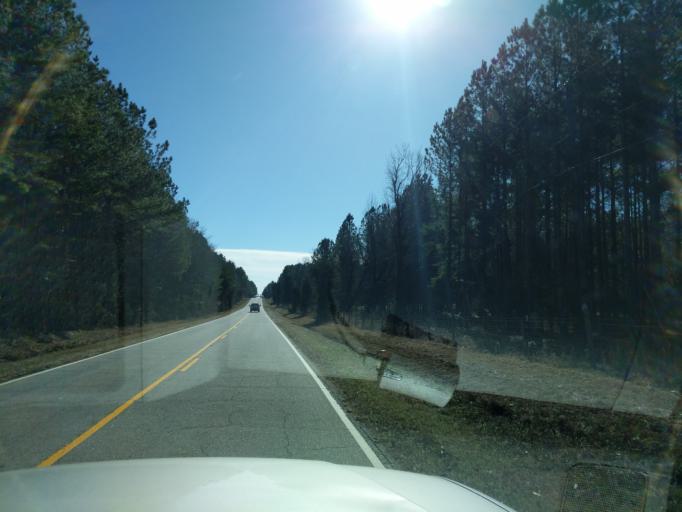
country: US
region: South Carolina
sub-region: Saluda County
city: Saluda
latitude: 34.1252
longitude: -81.8392
